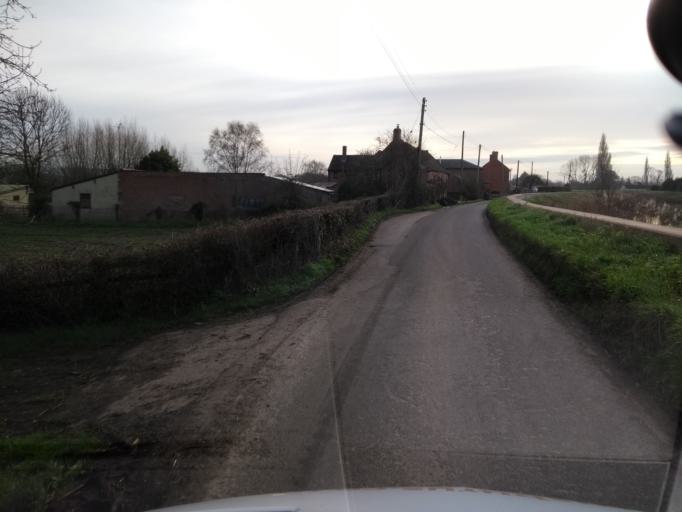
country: GB
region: England
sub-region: Somerset
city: Westonzoyland
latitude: 51.0735
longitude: -2.9237
